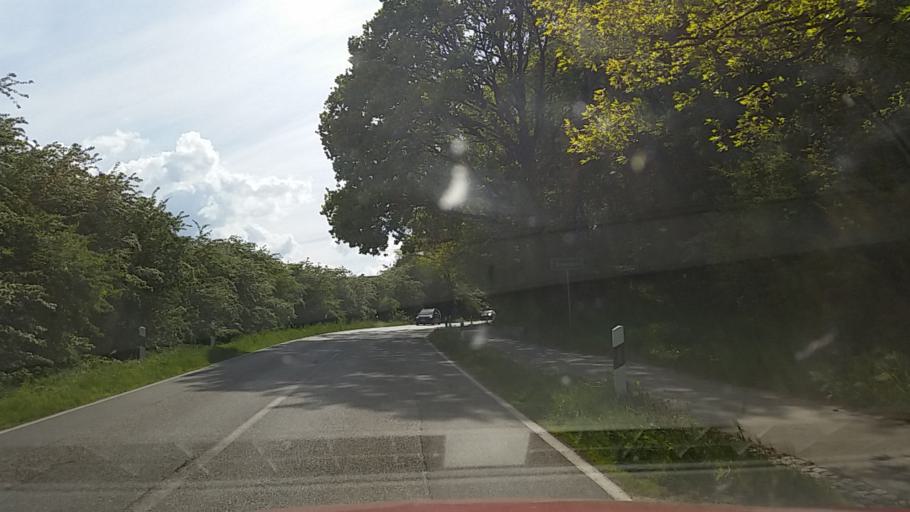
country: DE
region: Schleswig-Holstein
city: Meddewade
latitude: 53.8172
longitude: 10.4286
